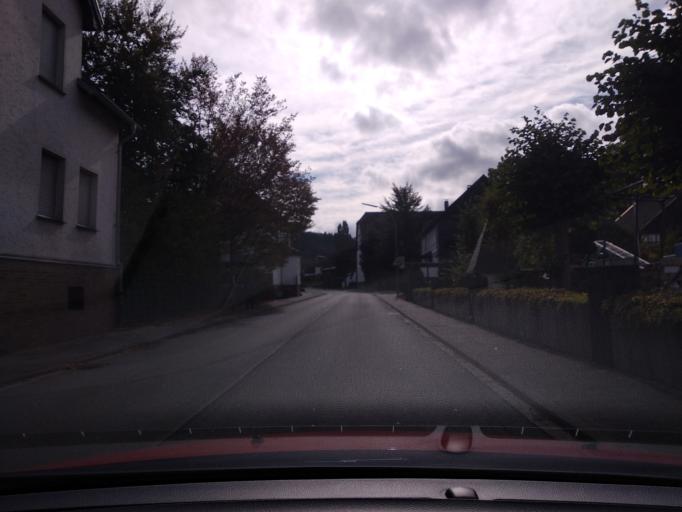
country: DE
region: North Rhine-Westphalia
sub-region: Regierungsbezirk Arnsberg
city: Bestwig
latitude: 51.3348
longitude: 8.4059
